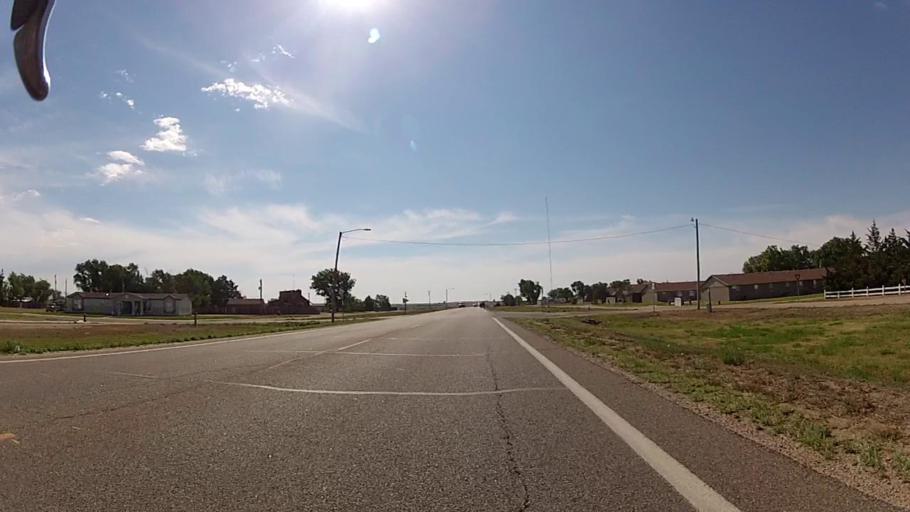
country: US
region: Kansas
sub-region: Grant County
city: Ulysses
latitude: 37.5743
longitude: -101.3427
